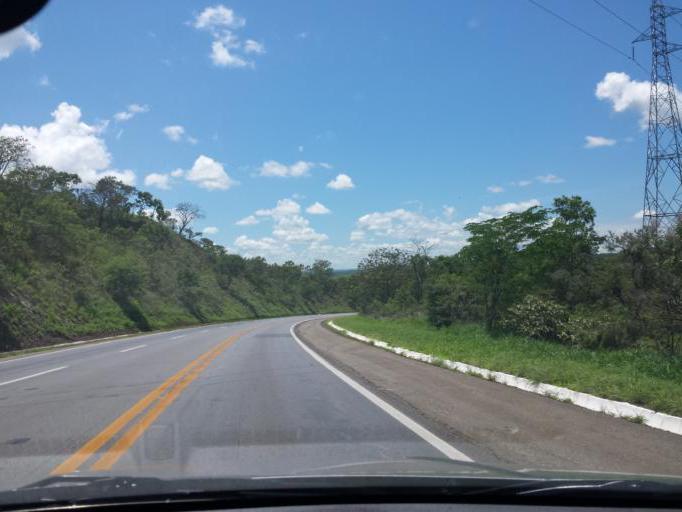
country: BR
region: Goias
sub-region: Luziania
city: Luziania
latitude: -16.3806
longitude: -47.8278
